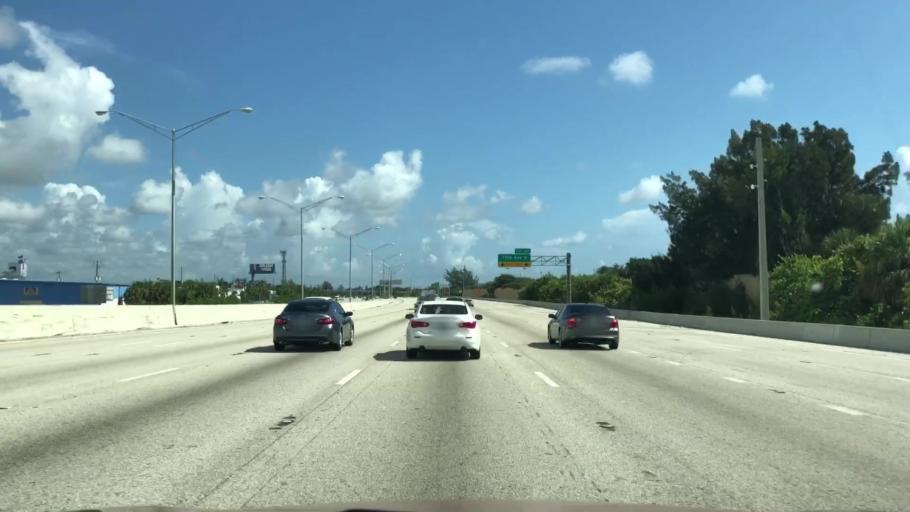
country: US
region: Florida
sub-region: Palm Beach County
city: Lake Worth
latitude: 26.6184
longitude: -80.0676
